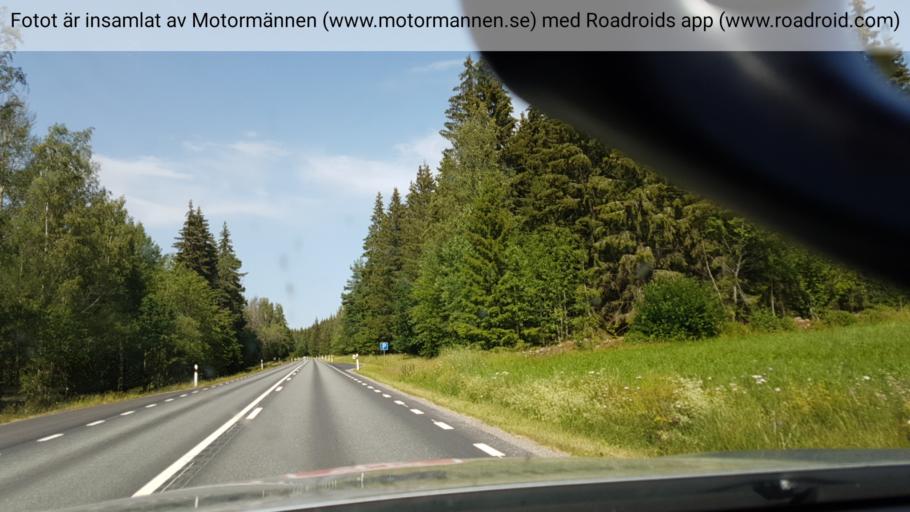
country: SE
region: Joenkoeping
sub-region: Aneby Kommun
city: Aneby
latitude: 57.8969
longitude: 14.8894
